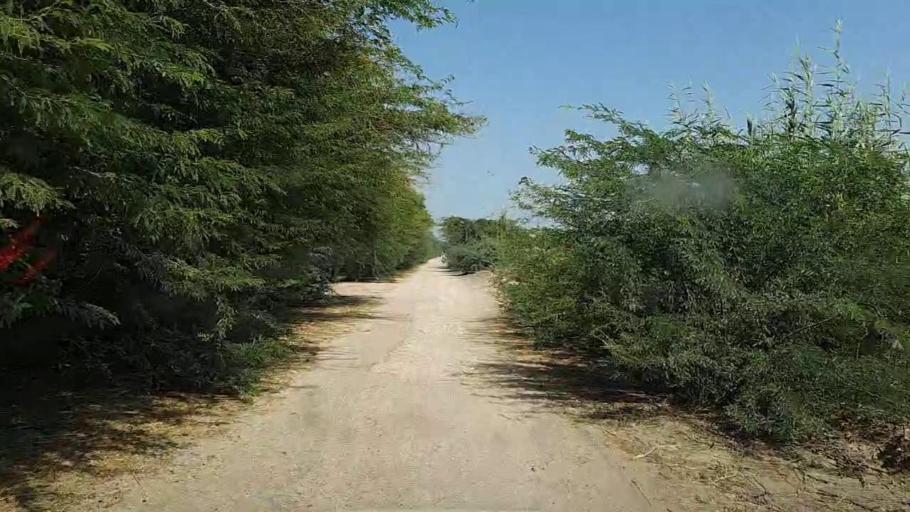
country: PK
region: Sindh
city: Mirpur Batoro
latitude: 24.7087
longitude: 68.4148
